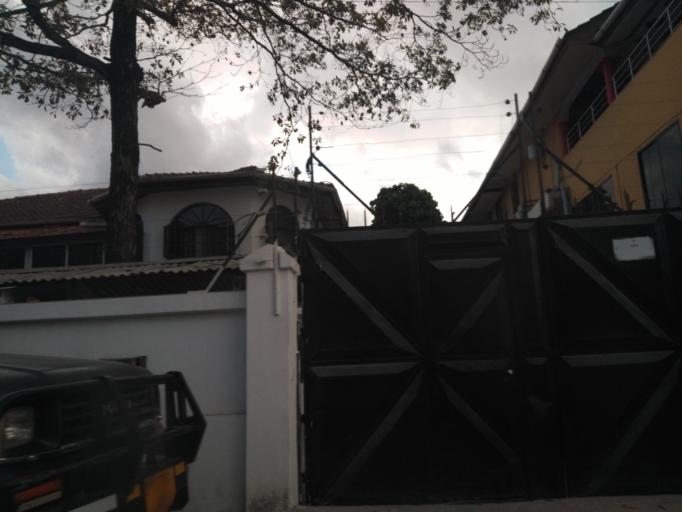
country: TZ
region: Dar es Salaam
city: Magomeni
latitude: -6.7633
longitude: 39.2685
